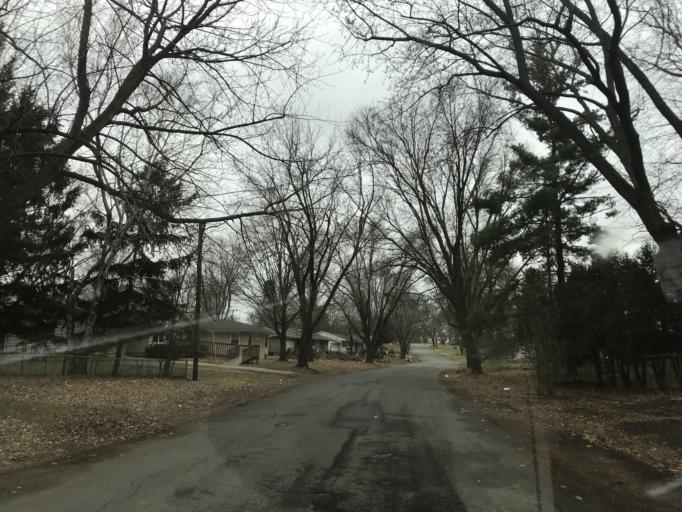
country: US
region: Wisconsin
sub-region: Dane County
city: Monona
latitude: 43.0698
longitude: -89.3130
